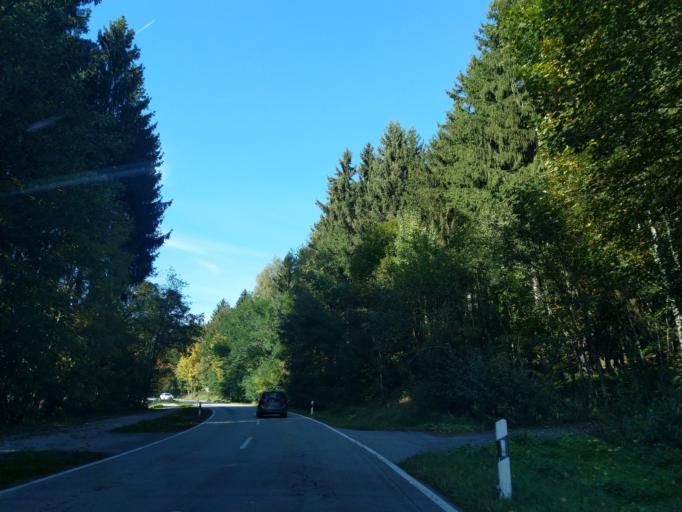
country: DE
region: Bavaria
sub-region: Lower Bavaria
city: Bernried
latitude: 48.9218
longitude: 12.9230
